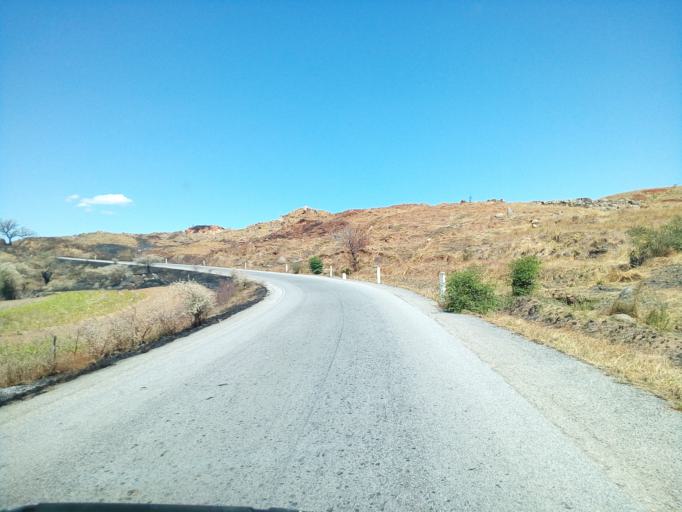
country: MG
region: Betsiboka
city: Maevatanana
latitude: -17.0810
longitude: 46.8063
